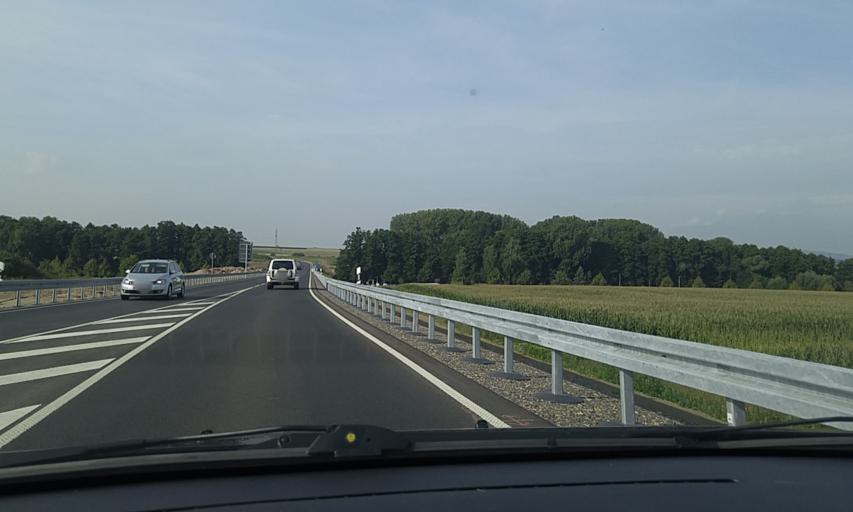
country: DE
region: Hesse
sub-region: Regierungsbezirk Darmstadt
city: Friedberg
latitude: 50.2909
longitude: 8.7642
